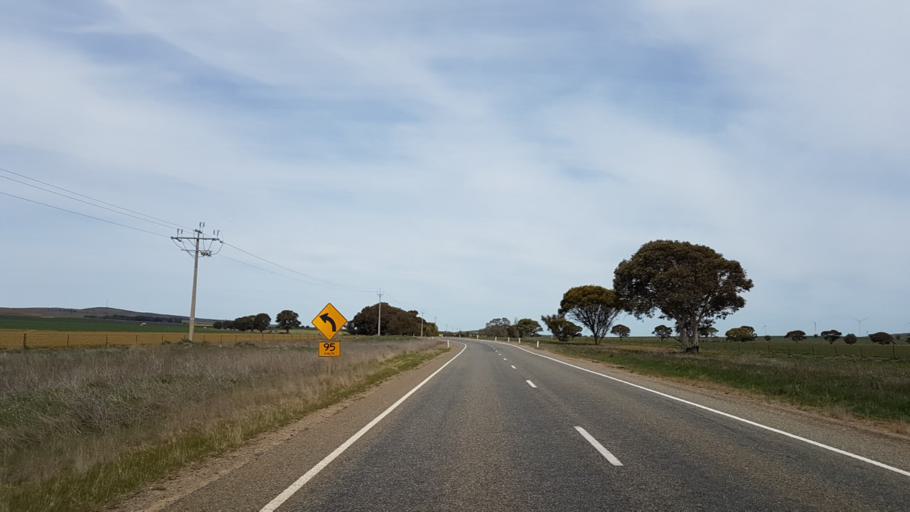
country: AU
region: South Australia
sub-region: Northern Areas
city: Jamestown
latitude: -33.0753
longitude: 138.6155
